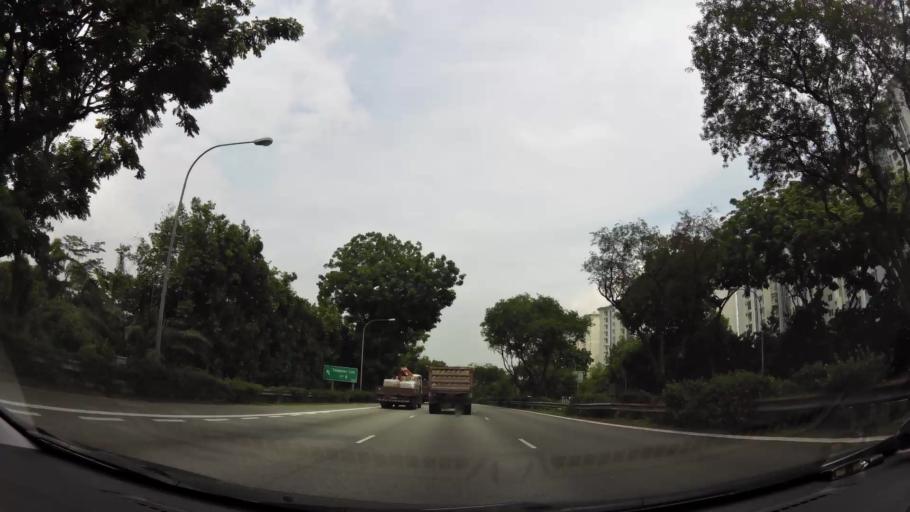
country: MY
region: Johor
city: Kampung Pasir Gudang Baru
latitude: 1.3696
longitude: 103.9425
